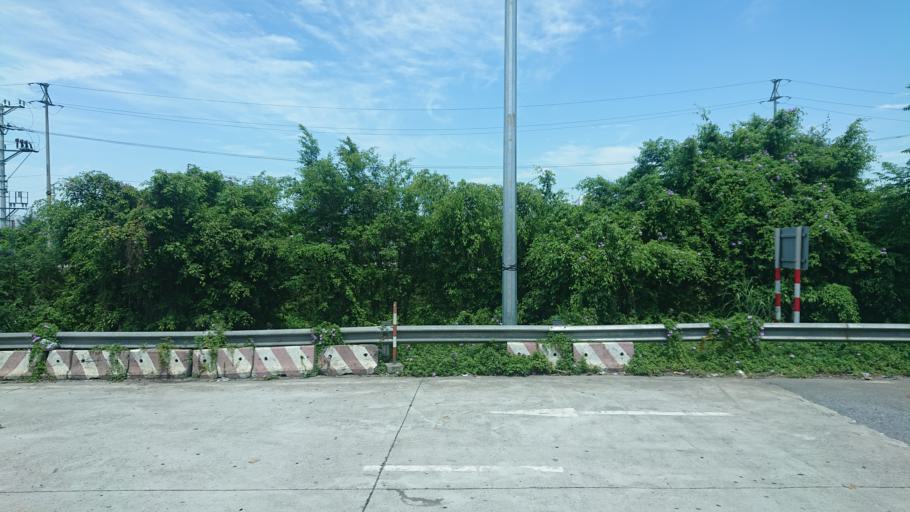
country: VN
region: Ha Nam
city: Thanh Pho Phu Ly
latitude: 20.5403
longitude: 105.9474
